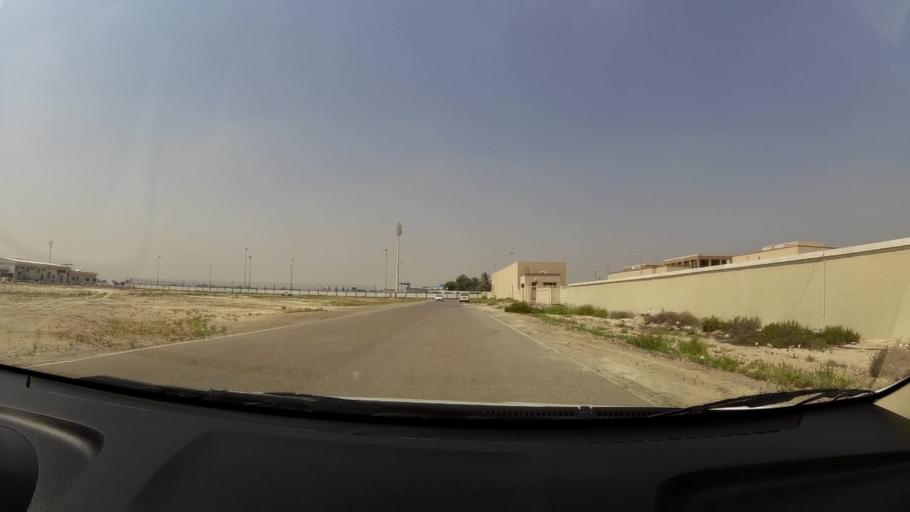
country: AE
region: Umm al Qaywayn
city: Umm al Qaywayn
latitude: 25.5694
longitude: 55.5615
